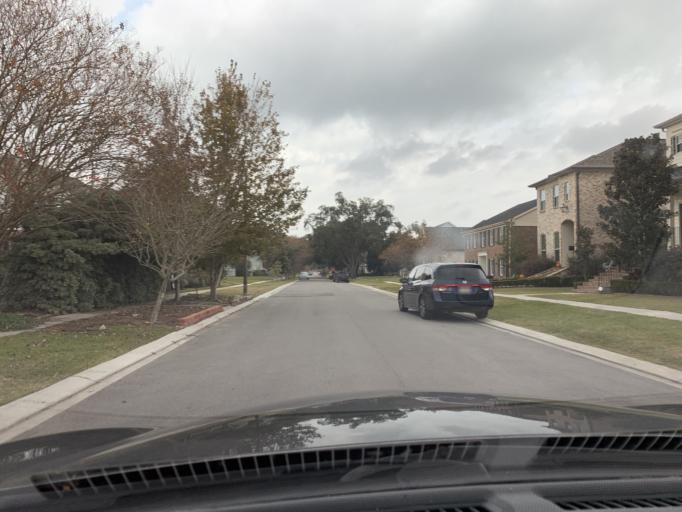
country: US
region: Louisiana
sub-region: Jefferson Parish
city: Metairie
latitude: 30.0138
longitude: -90.1004
